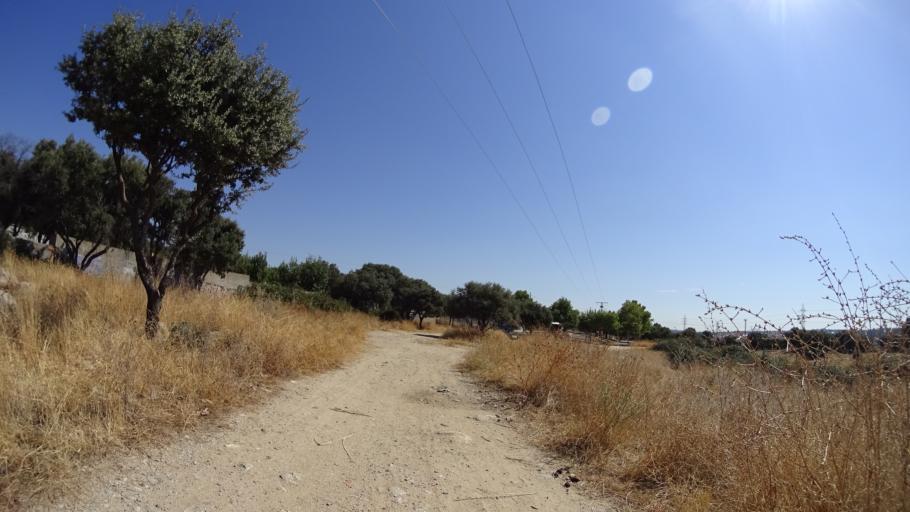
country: ES
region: Madrid
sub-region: Provincia de Madrid
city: Galapagar
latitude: 40.5990
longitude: -4.0118
